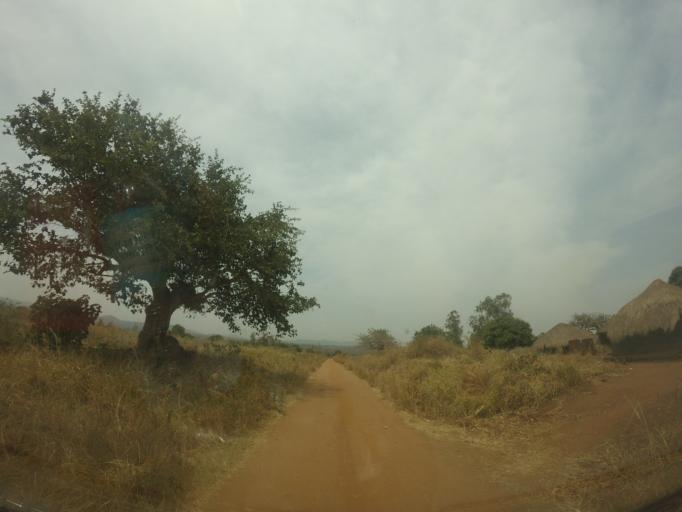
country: UG
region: Northern Region
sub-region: Nebbi District
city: Nebbi
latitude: 2.6195
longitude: 31.0424
